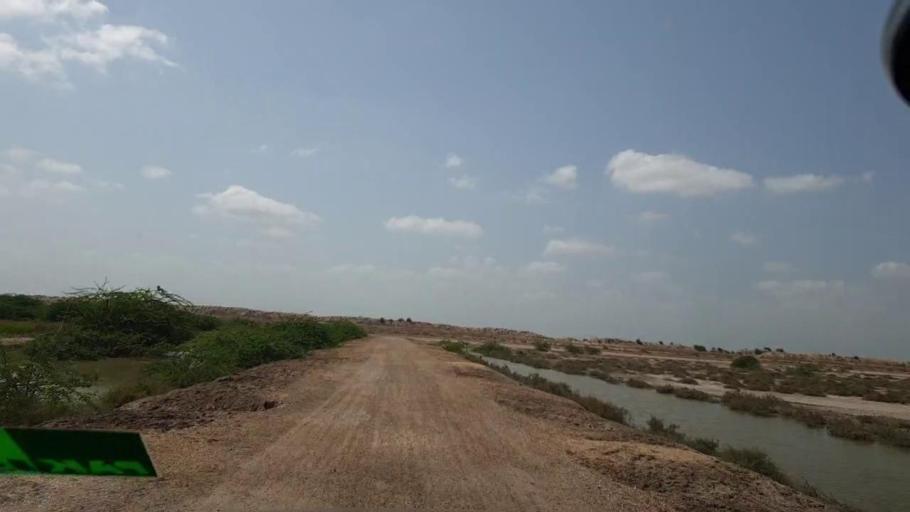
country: PK
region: Sindh
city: Kadhan
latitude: 24.5987
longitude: 69.1848
